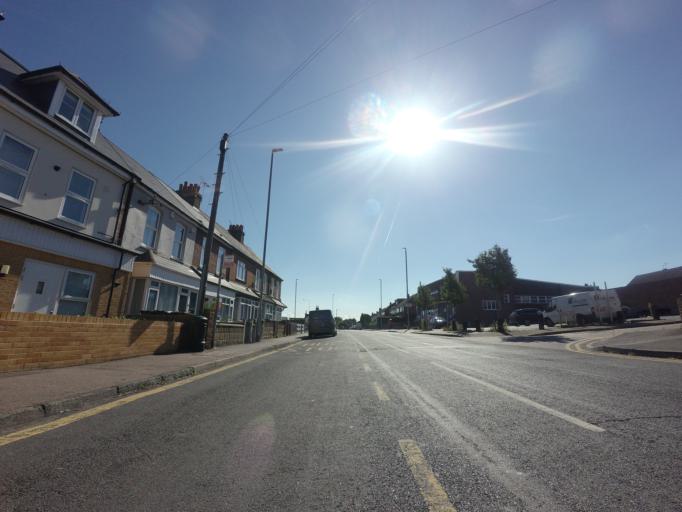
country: GB
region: England
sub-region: Kent
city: Gravesend
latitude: 51.4318
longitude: 0.3997
